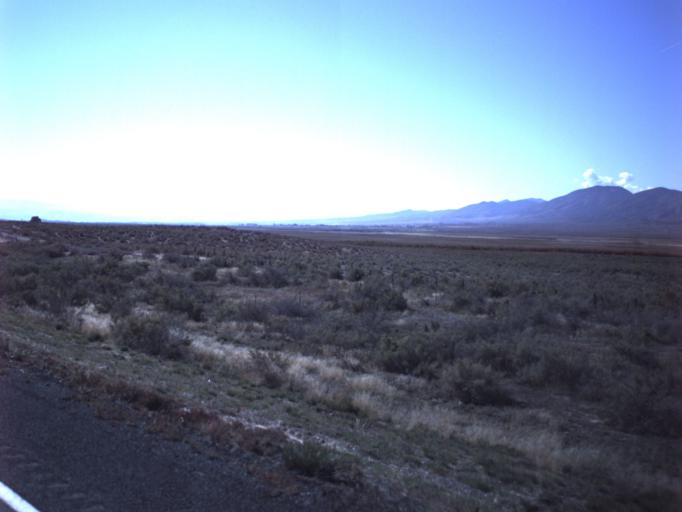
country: US
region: Utah
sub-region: Sanpete County
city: Gunnison
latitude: 39.2930
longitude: -111.8883
